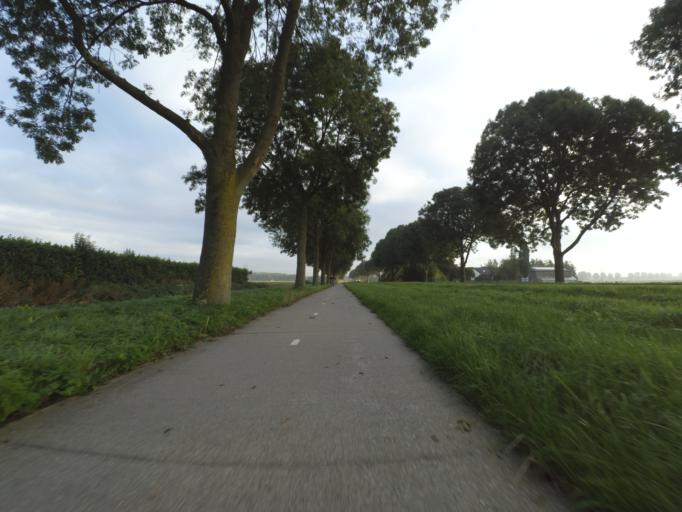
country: NL
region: Flevoland
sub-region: Gemeente Dronten
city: Dronten
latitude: 52.5096
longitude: 5.6853
